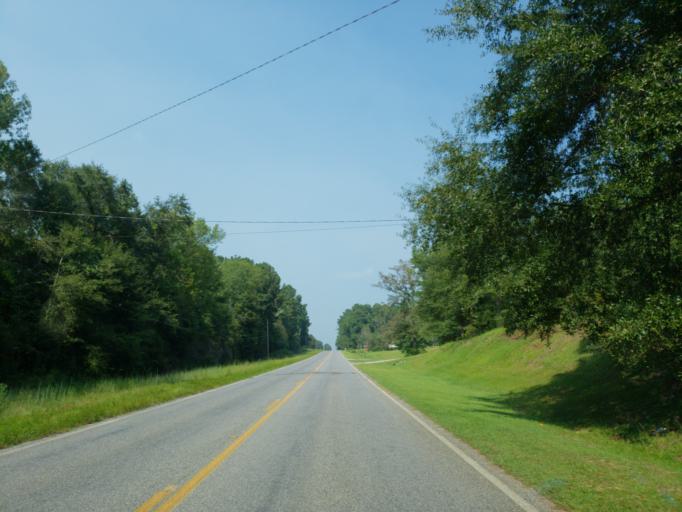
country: US
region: Mississippi
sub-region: Jones County
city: Sharon
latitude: 31.8843
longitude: -88.9546
